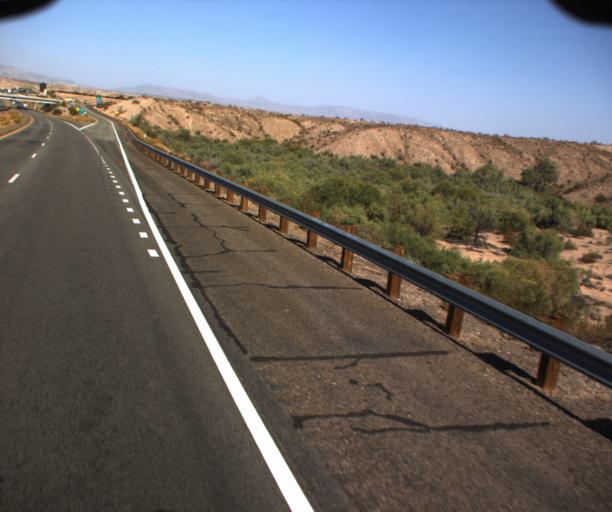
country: US
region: California
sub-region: San Bernardino County
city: Needles
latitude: 34.7185
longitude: -114.4740
